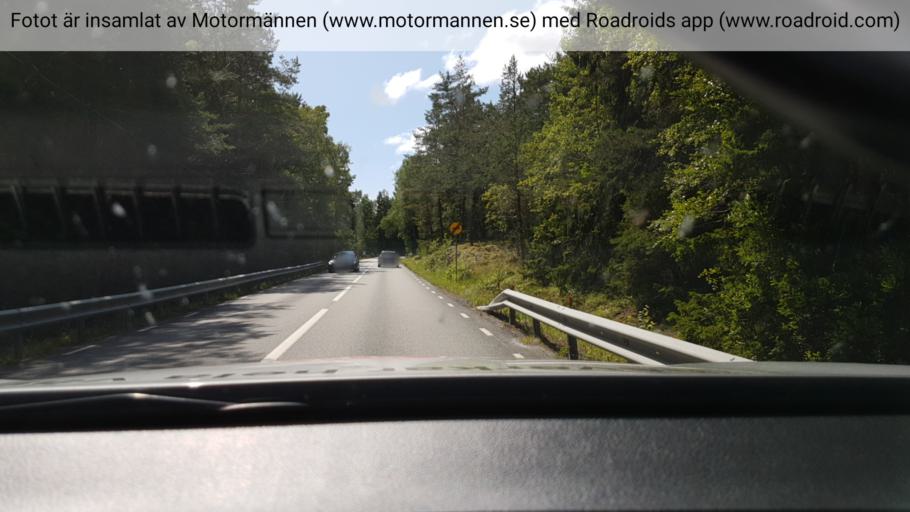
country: SE
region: Stockholm
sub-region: Norrtalje Kommun
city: Arno
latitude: 60.0901
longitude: 18.7918
